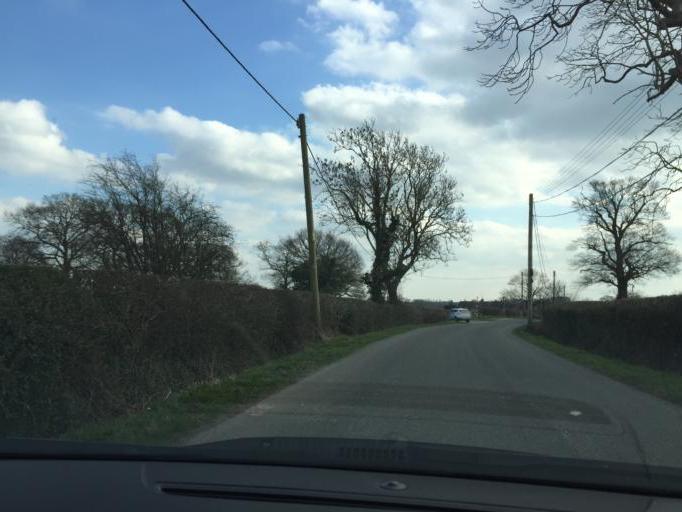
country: GB
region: England
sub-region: Coventry
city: Keresley
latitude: 52.4409
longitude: -1.5721
